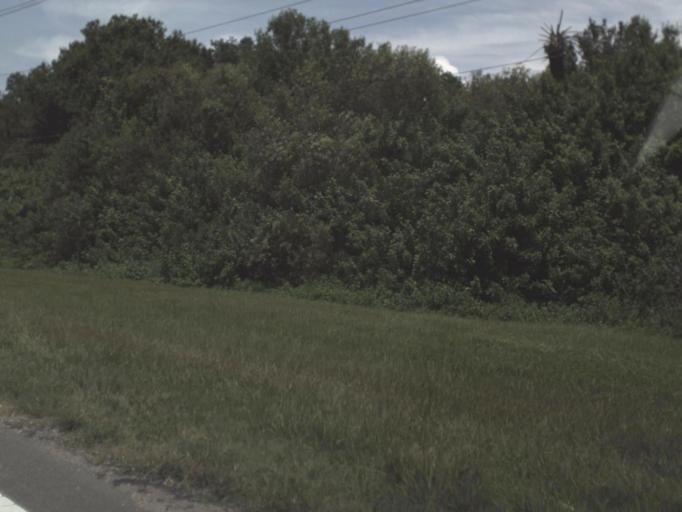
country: US
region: Florida
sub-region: Hillsborough County
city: Apollo Beach
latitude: 27.7925
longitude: -82.3783
